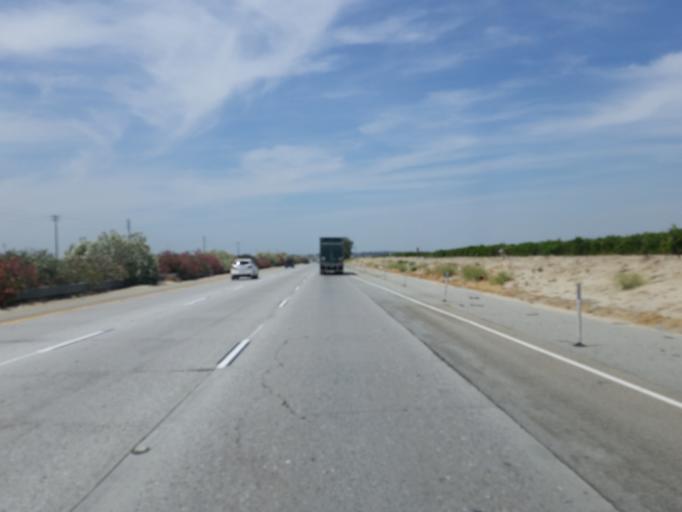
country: US
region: California
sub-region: Kern County
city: Weedpatch
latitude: 35.1276
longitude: -118.9898
